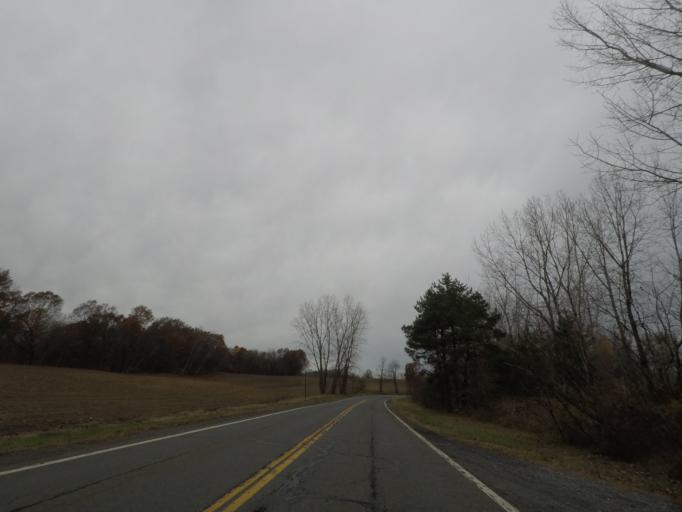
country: US
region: New York
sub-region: Saratoga County
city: Mechanicville
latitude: 42.8511
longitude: -73.6986
